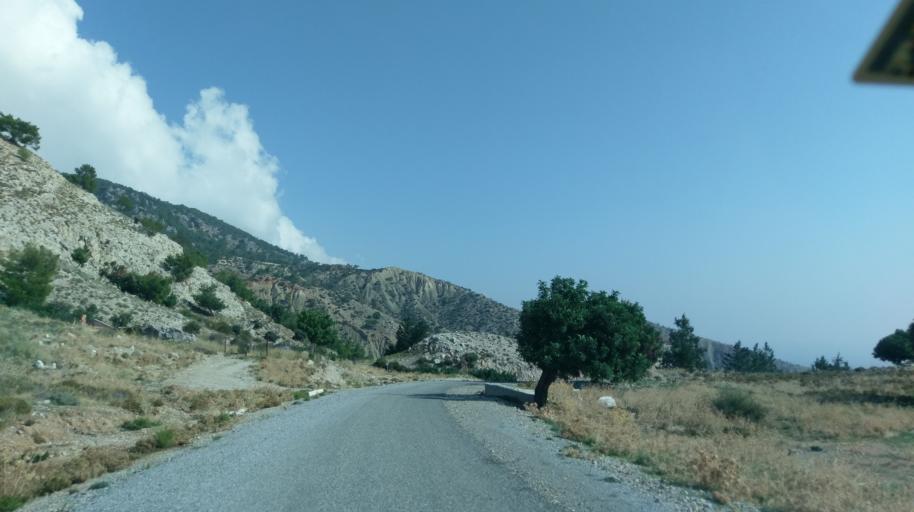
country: CY
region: Ammochostos
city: Lefkonoiko
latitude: 35.2874
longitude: 33.5661
